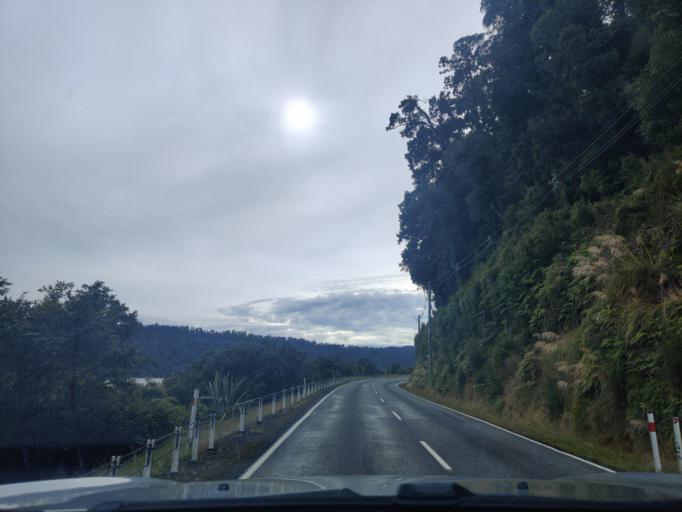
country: NZ
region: West Coast
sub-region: Westland District
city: Hokitika
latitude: -43.2527
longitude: 170.2536
